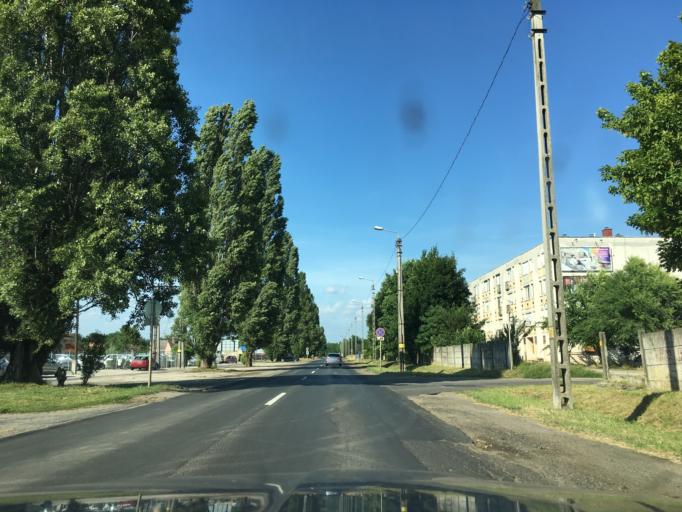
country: HU
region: Hajdu-Bihar
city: Debrecen
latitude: 47.5548
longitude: 21.6673
